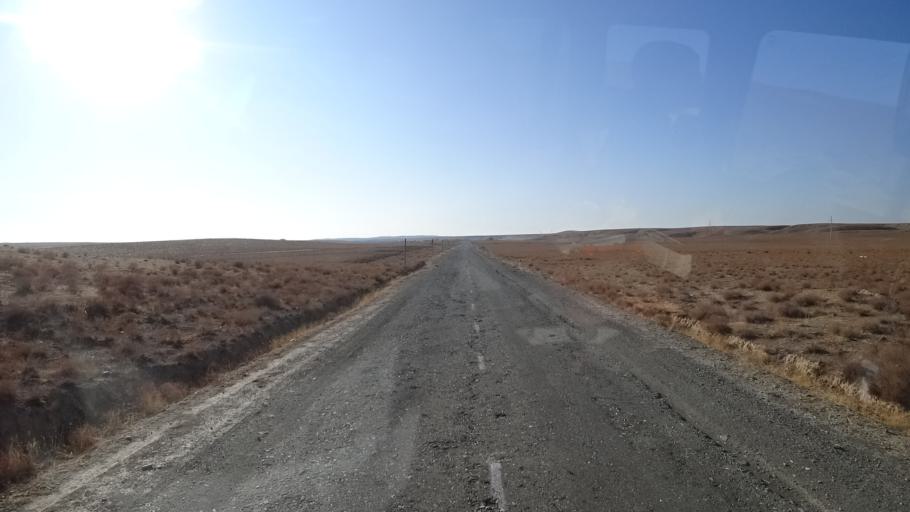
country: UZ
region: Navoiy
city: Beshrabot
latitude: 40.2584
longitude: 65.4718
